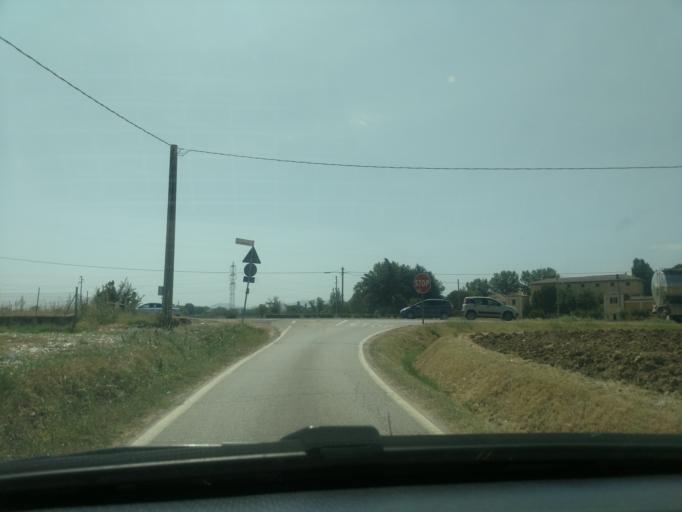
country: IT
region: Emilia-Romagna
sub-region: Provincia di Bologna
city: Villanova
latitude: 44.4840
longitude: 11.4542
